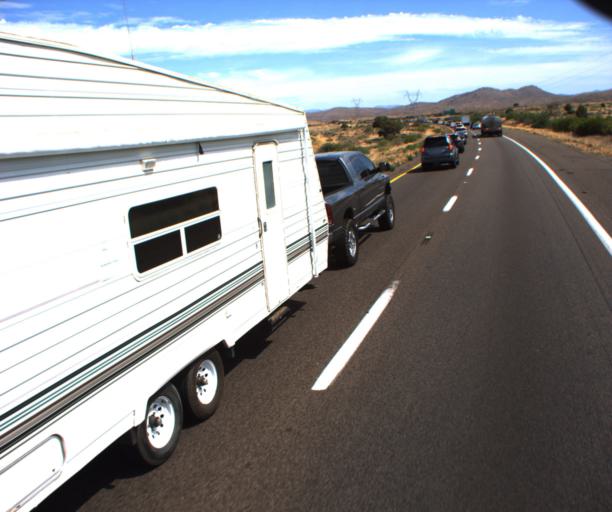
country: US
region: Arizona
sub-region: Yavapai County
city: Cordes Lakes
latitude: 34.2163
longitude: -112.1115
